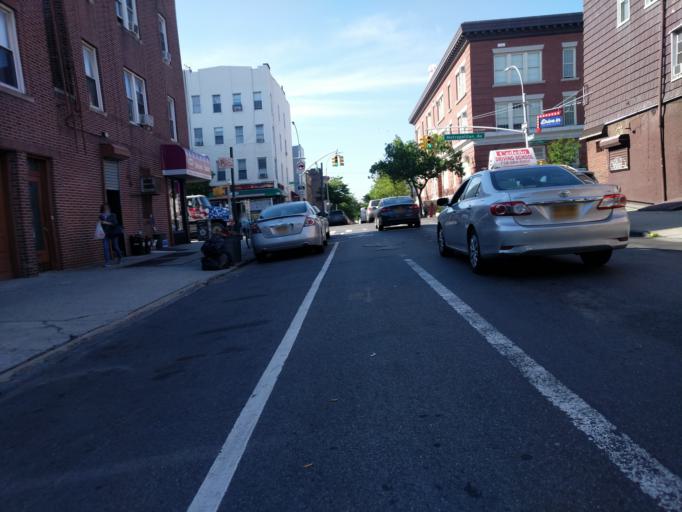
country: US
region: New York
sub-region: Queens County
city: Long Island City
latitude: 40.7140
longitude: -73.9461
